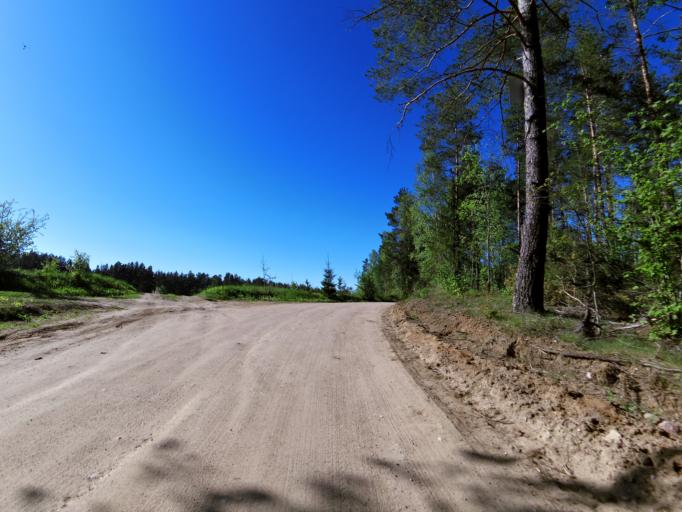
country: LT
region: Vilnius County
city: Pilaite
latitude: 54.6891
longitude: 25.1621
